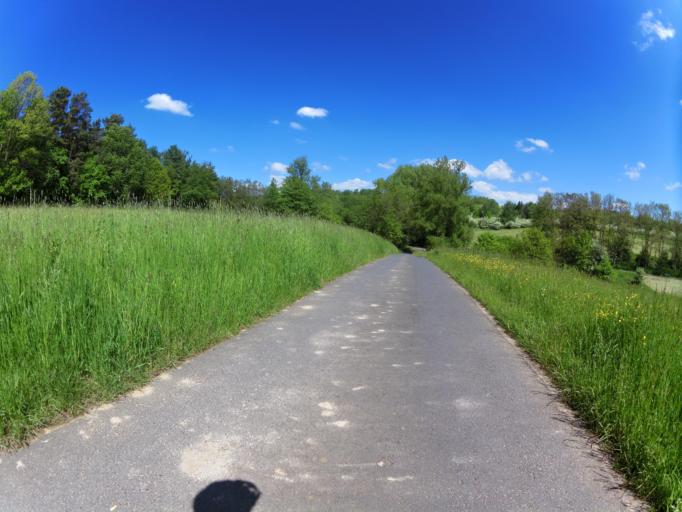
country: DE
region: Thuringia
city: Dankmarshausen
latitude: 50.9543
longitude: 10.0384
